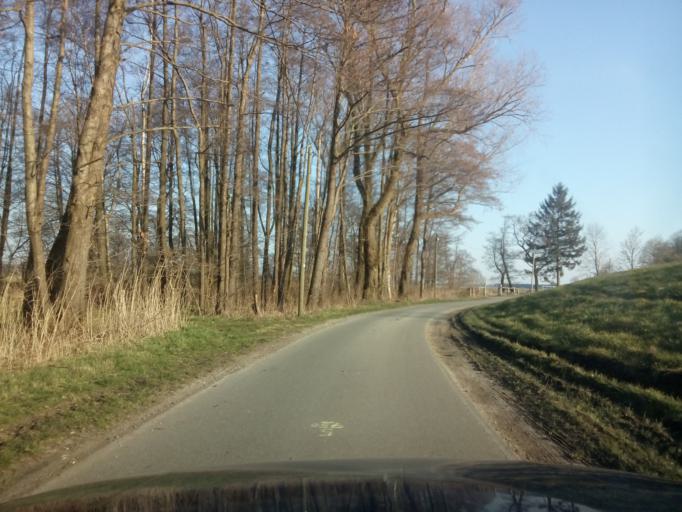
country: DE
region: Lower Saxony
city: Lilienthal
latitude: 53.1583
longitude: 8.8397
